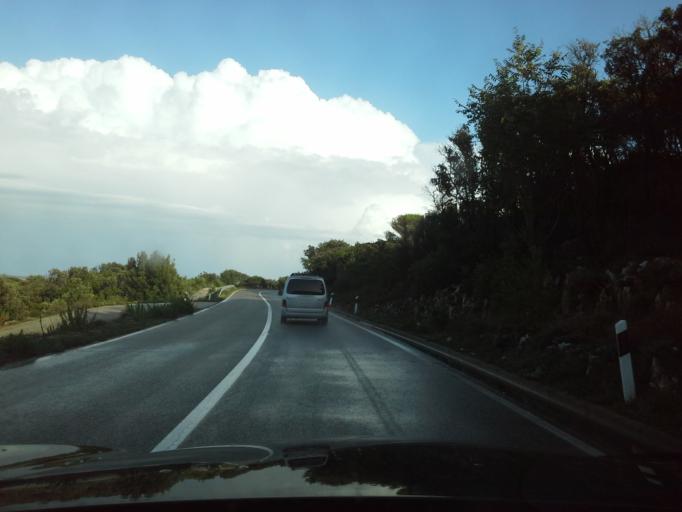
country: HR
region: Primorsko-Goranska
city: Mali Losinj
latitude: 44.6112
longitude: 14.3988
